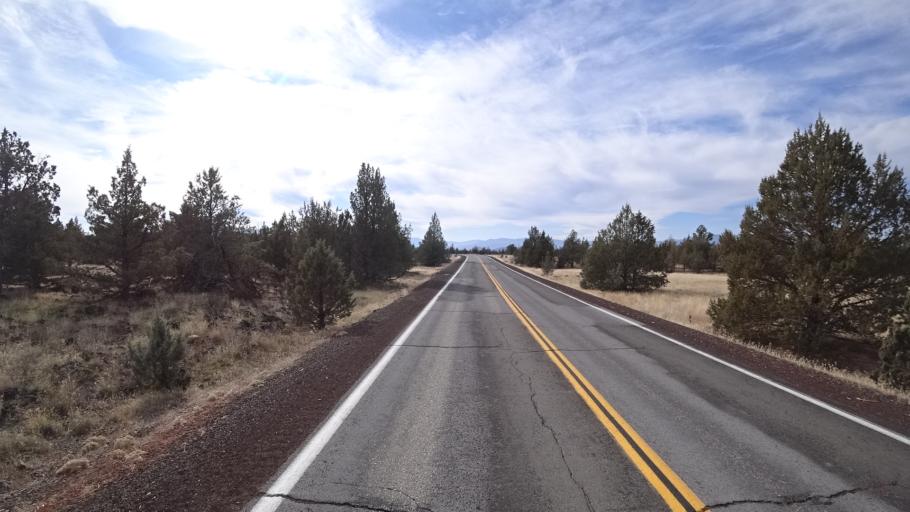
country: US
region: California
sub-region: Siskiyou County
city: Weed
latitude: 41.5930
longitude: -122.3974
